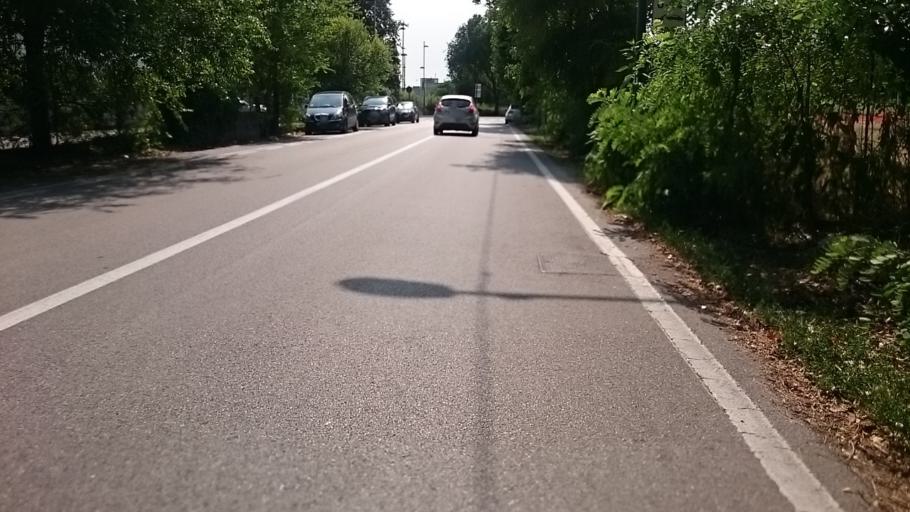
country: IT
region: Veneto
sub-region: Provincia di Venezia
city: Mestre
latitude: 45.4828
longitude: 12.2467
